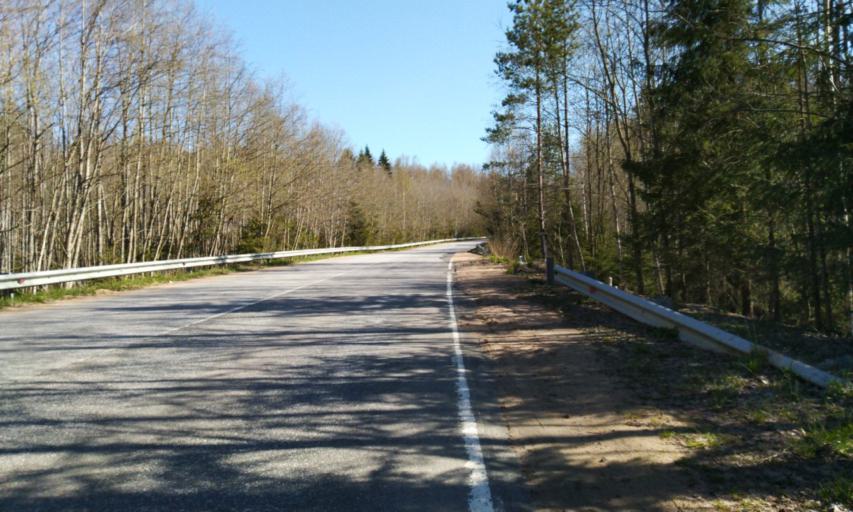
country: RU
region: Leningrad
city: Garbolovo
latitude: 60.3710
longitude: 30.4421
